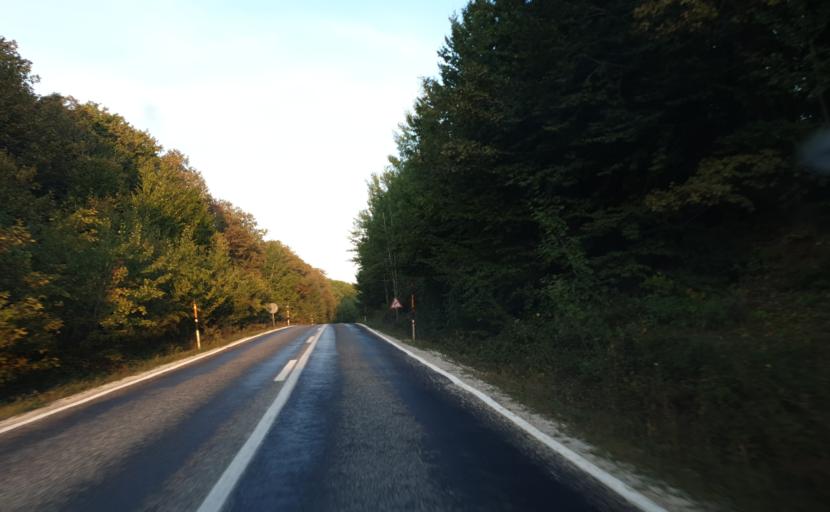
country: TR
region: Kirklareli
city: Igneada
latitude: 41.8756
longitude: 27.8252
